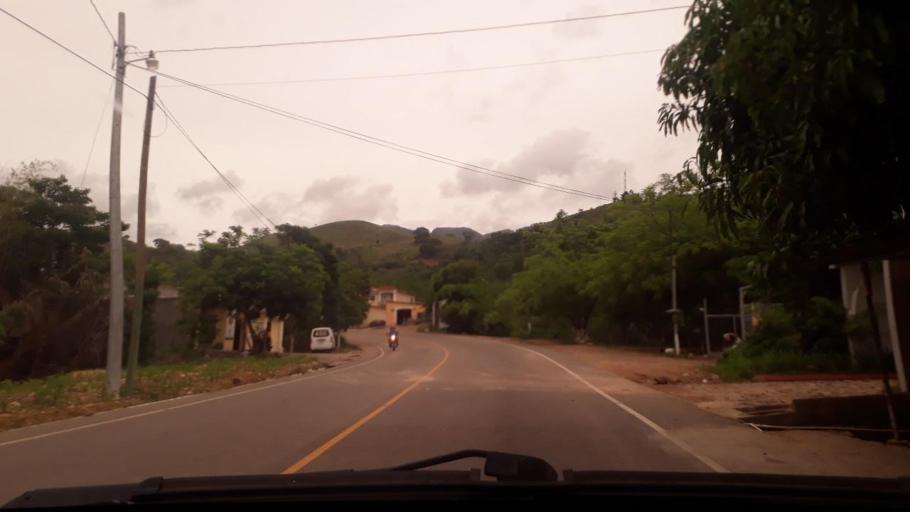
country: GT
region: Chiquimula
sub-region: Municipio de Jocotan
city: Jocotan
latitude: 14.8169
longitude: -89.3763
